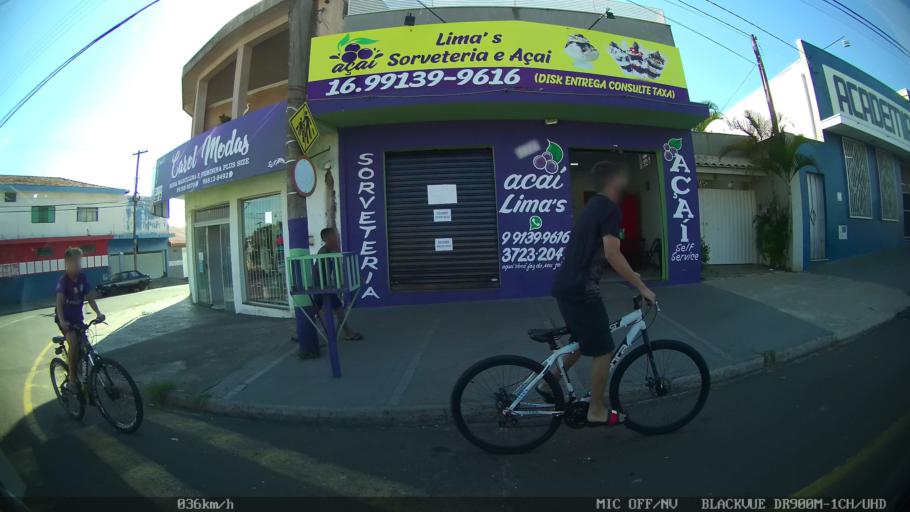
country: BR
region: Sao Paulo
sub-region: Franca
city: Franca
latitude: -20.4894
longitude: -47.4250
